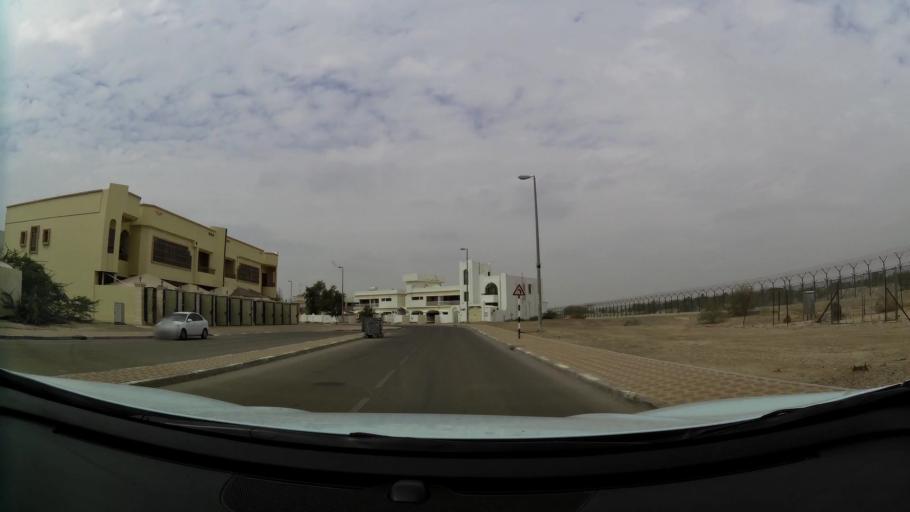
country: OM
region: Al Buraimi
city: Al Buraymi
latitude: 24.2275
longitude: 55.7869
